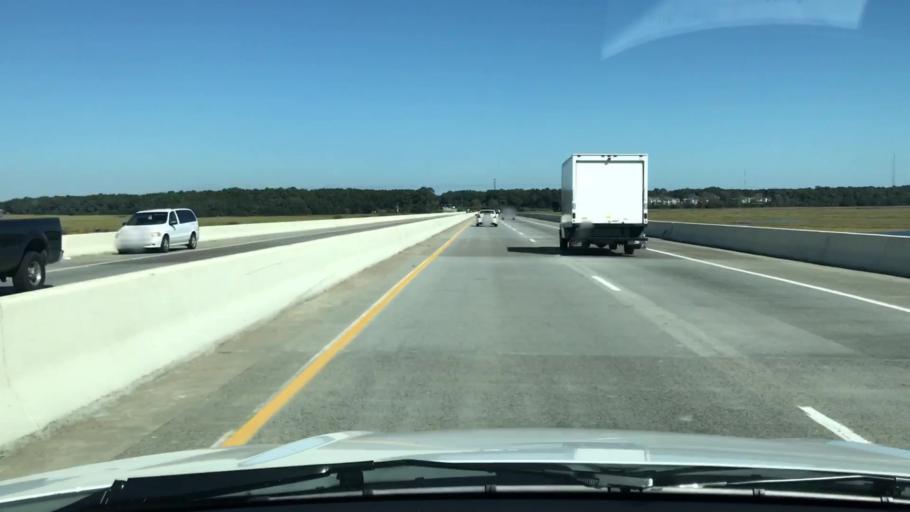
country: US
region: South Carolina
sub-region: Beaufort County
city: Shell Point
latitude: 32.3880
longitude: -80.7779
